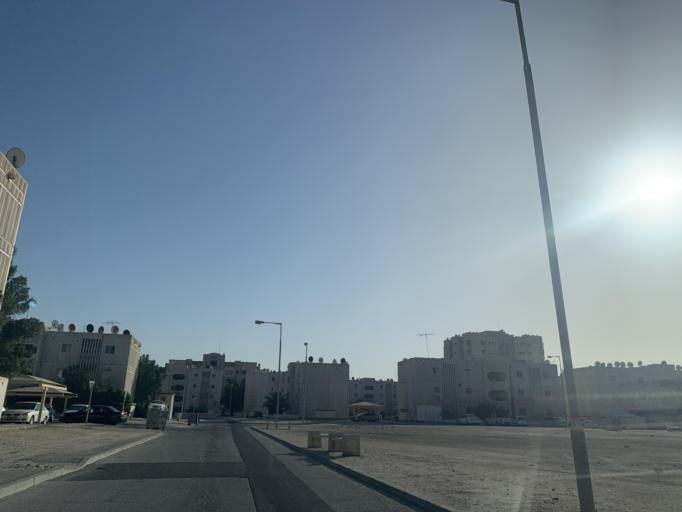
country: BH
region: Manama
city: Manama
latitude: 26.2023
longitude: 50.5869
